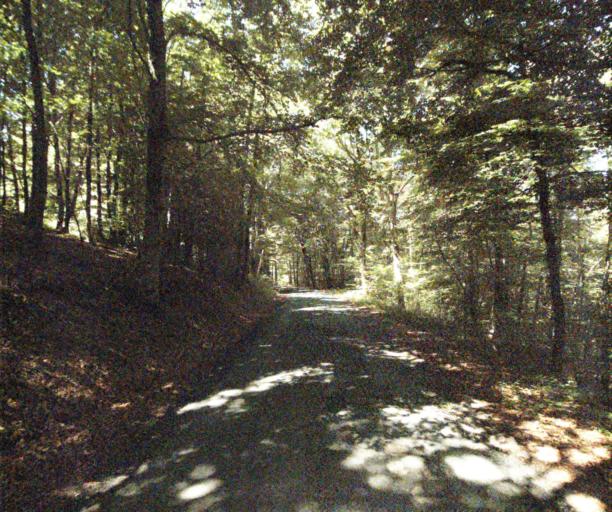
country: FR
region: Midi-Pyrenees
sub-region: Departement du Tarn
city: Dourgne
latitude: 43.4222
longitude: 2.1710
